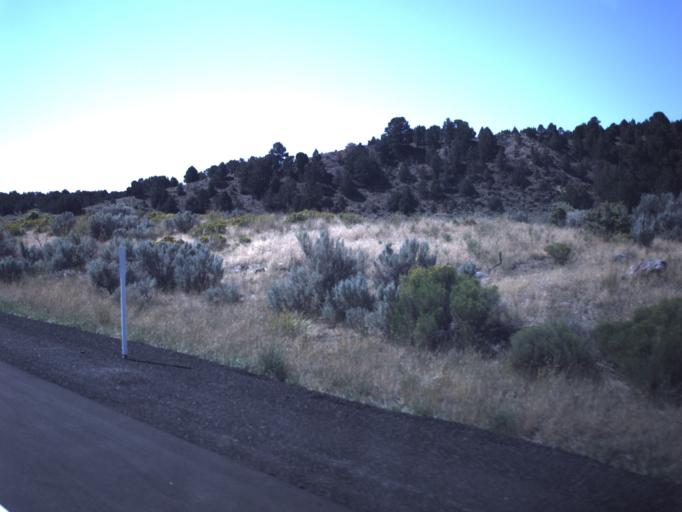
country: US
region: Utah
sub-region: Utah County
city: Eagle Mountain
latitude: 39.9908
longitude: -112.2675
